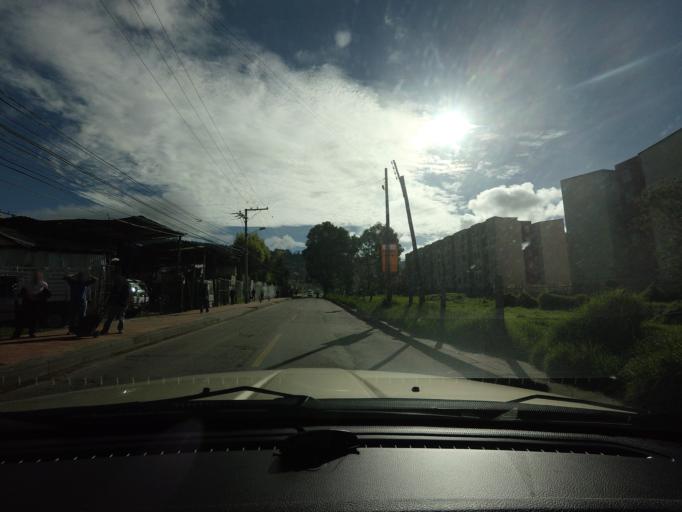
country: CO
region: Cundinamarca
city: La Calera
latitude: 4.7603
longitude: -74.0359
